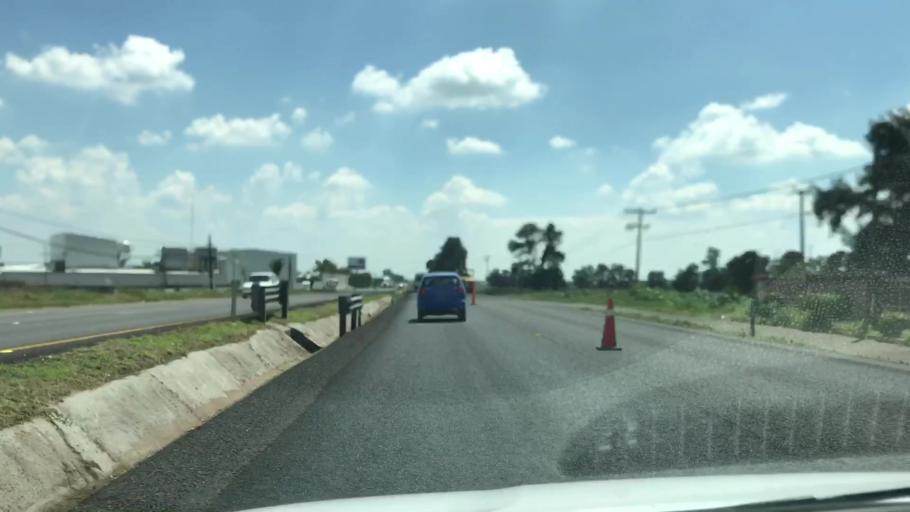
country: MX
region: Guanajuato
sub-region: Irapuato
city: San Jose de Bernalejo (El Guayabo)
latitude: 20.6199
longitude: -101.4005
